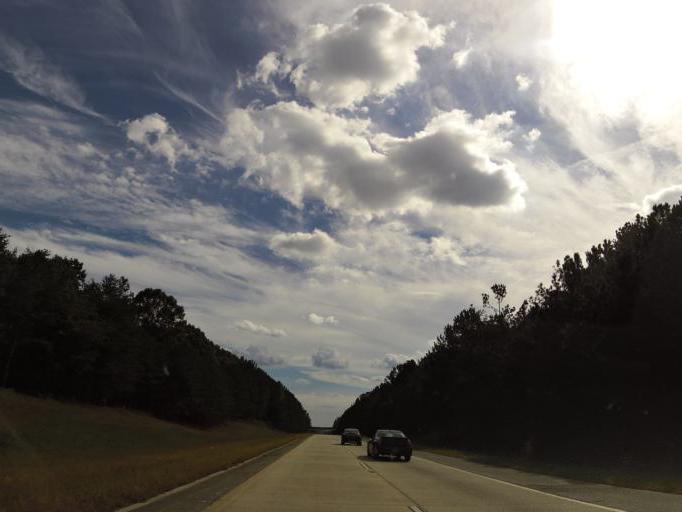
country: US
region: Georgia
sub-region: Pickens County
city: Nelson
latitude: 34.3642
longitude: -84.3916
